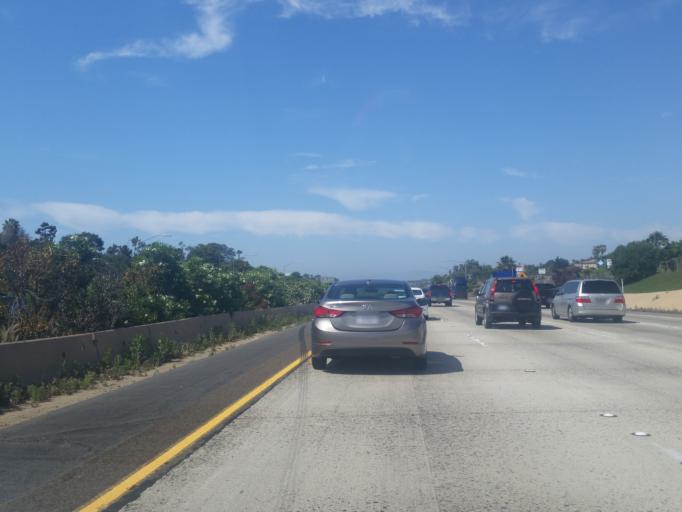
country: US
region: California
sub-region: San Diego County
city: Encinitas
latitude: 33.0660
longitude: -117.2924
